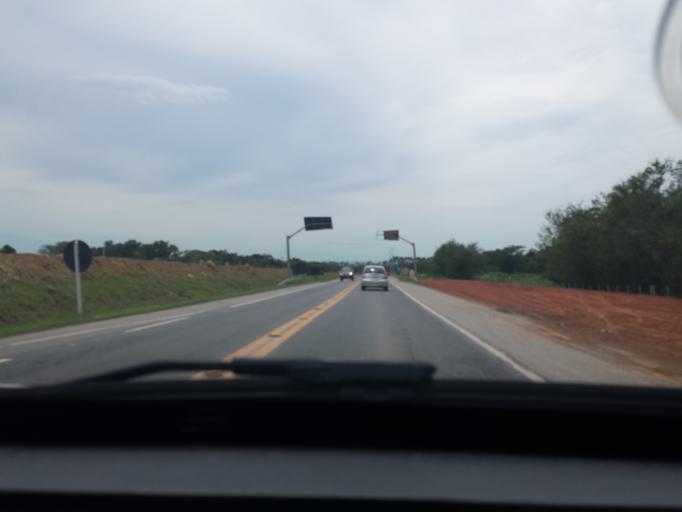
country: BR
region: Santa Catarina
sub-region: Gaspar
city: Gaspar
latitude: -26.8805
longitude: -48.8409
